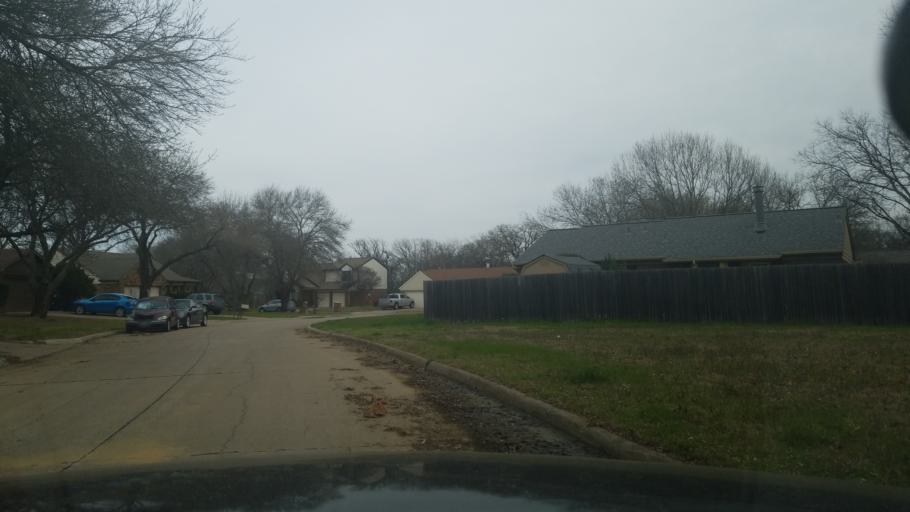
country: US
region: Texas
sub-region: Denton County
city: Hickory Creek
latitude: 33.1337
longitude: -97.0489
